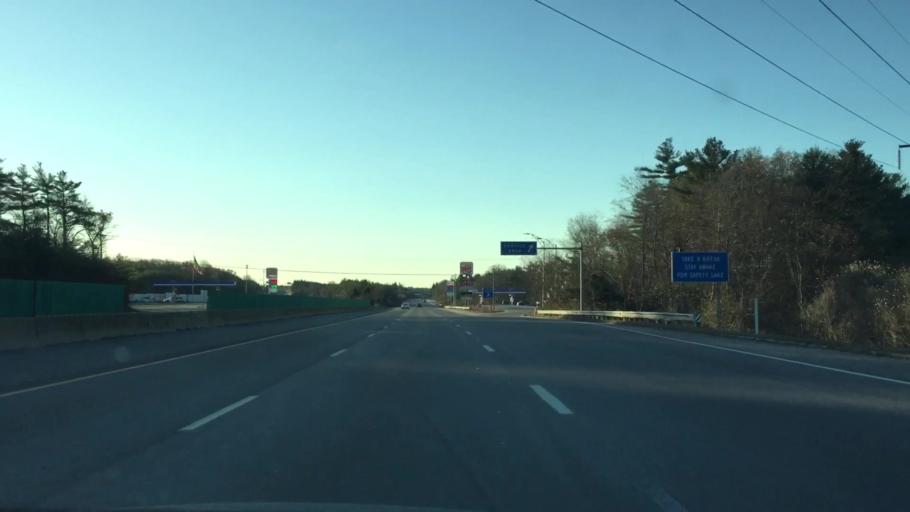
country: US
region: Massachusetts
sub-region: Bristol County
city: Raynham Center
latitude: 41.9586
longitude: -71.0276
